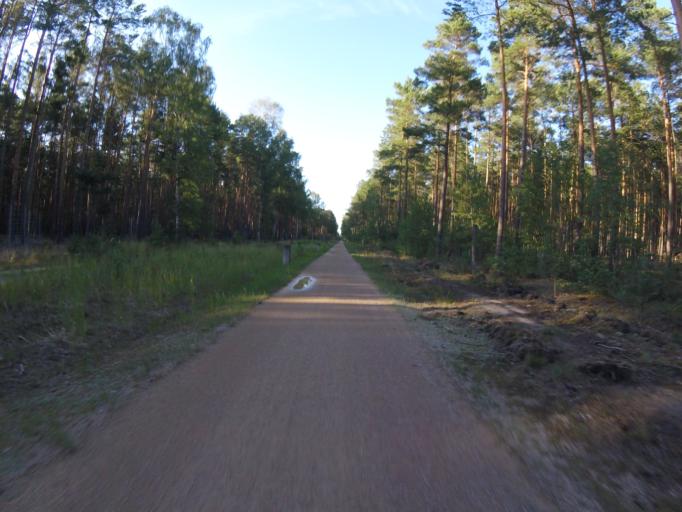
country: DE
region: Brandenburg
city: Halbe
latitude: 52.1888
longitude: 13.7604
